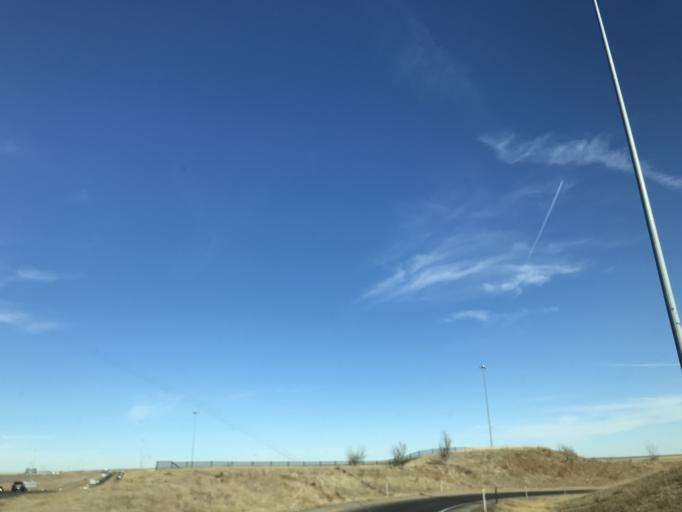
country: US
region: Colorado
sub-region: Adams County
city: Aurora
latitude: 39.8358
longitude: -104.7467
